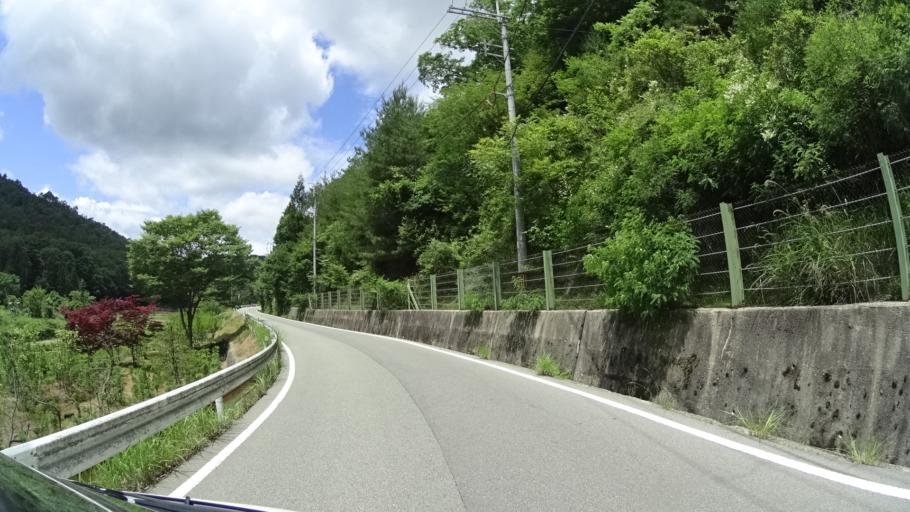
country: JP
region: Hyogo
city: Sasayama
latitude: 35.0219
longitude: 135.3955
